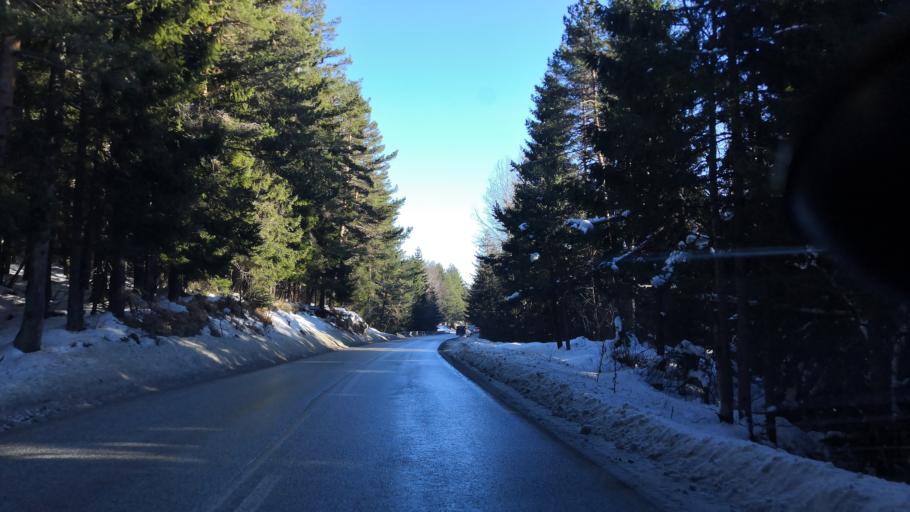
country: BA
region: Republika Srpska
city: Sokolac
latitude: 43.9252
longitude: 18.6688
